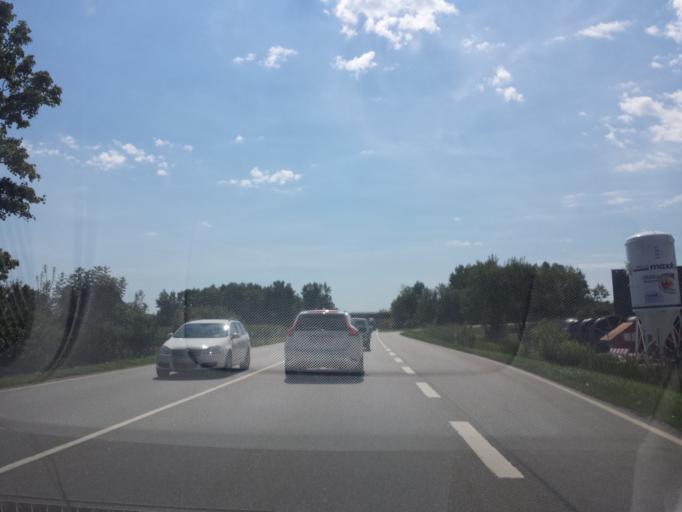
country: DE
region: Bavaria
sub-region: Lower Bavaria
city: Steinach
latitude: 48.9523
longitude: 12.6221
